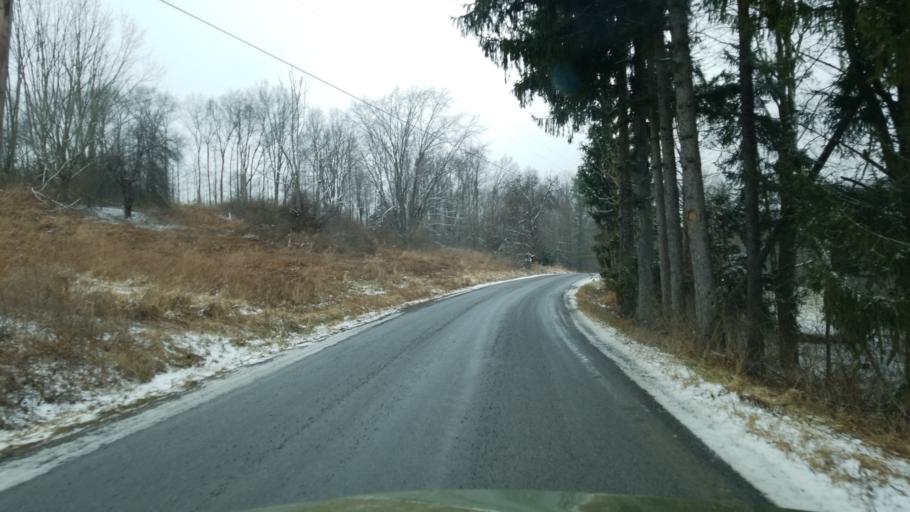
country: US
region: Pennsylvania
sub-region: Jefferson County
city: Sykesville
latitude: 41.0436
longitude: -78.7849
